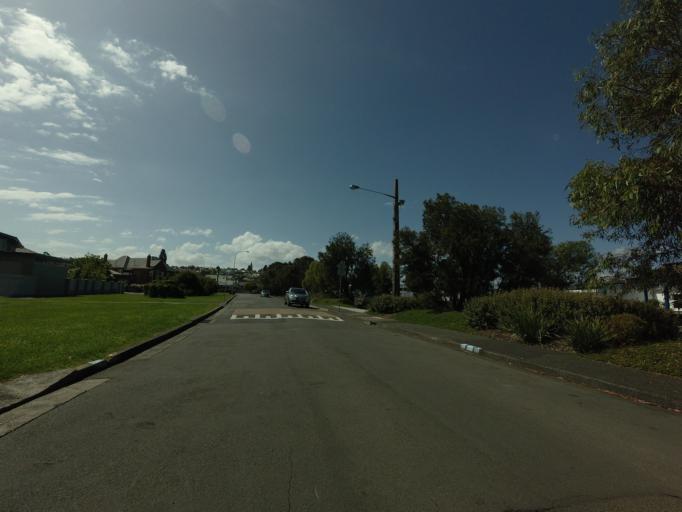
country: AU
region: Tasmania
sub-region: Hobart
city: Sandy Bay
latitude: -42.8977
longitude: 147.3319
